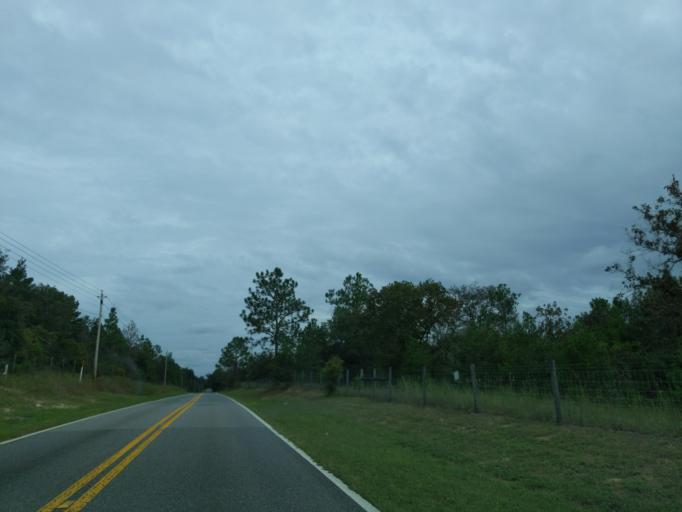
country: US
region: Florida
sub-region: Leon County
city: Woodville
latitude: 30.3739
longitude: -84.2060
